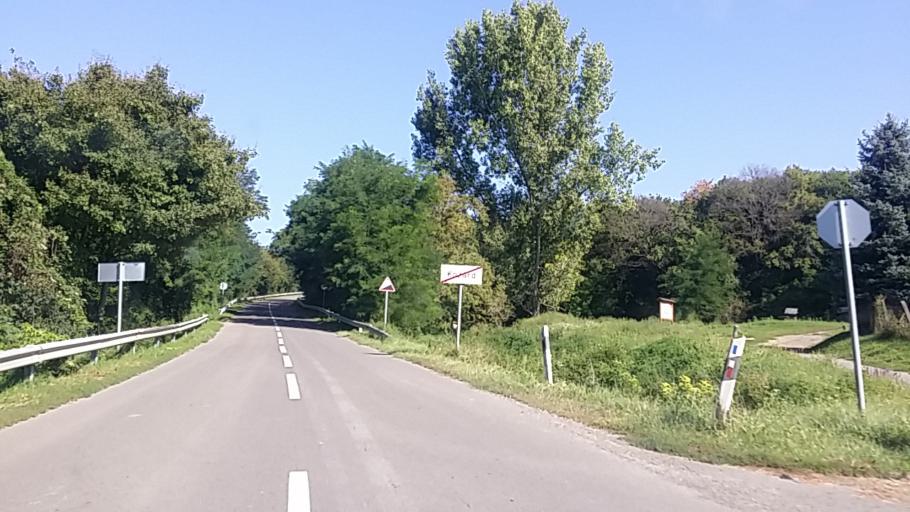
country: HU
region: Nograd
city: Paszto
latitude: 47.9172
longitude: 19.6201
